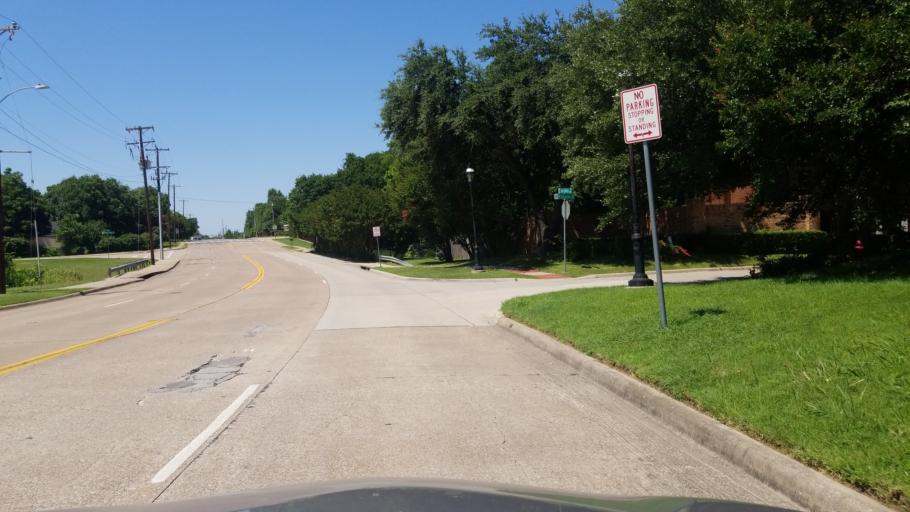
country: US
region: Texas
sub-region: Dallas County
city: Grand Prairie
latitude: 32.6870
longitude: -97.0032
